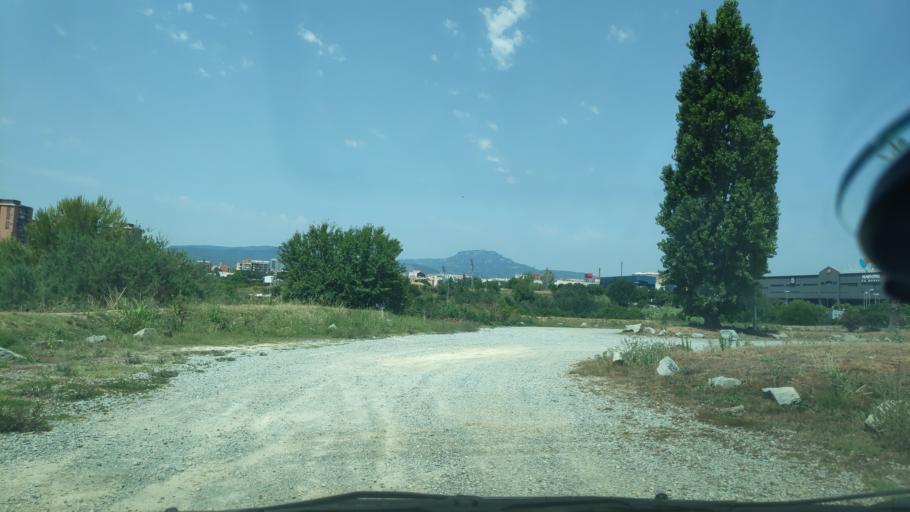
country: ES
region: Catalonia
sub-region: Provincia de Barcelona
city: Terrassa
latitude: 41.5439
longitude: 2.0231
